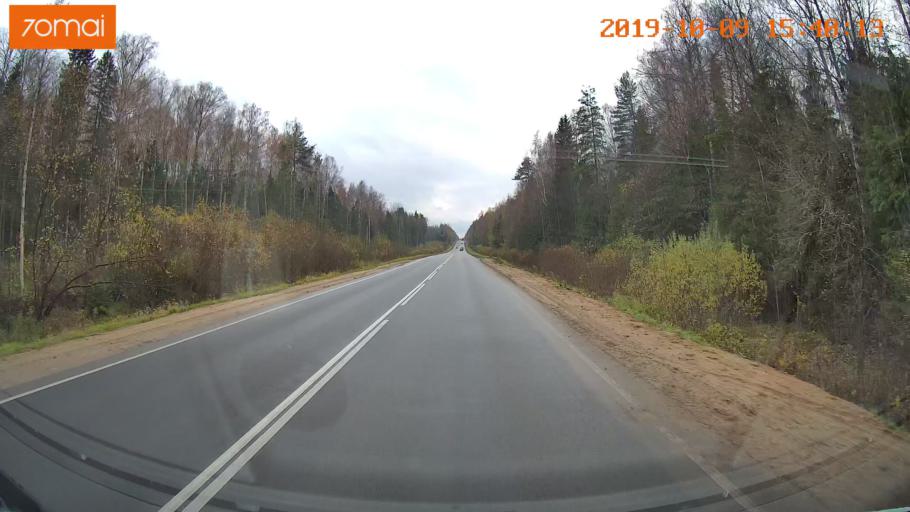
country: RU
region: Kostroma
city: Oktyabr'skiy
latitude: 57.8898
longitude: 41.1490
